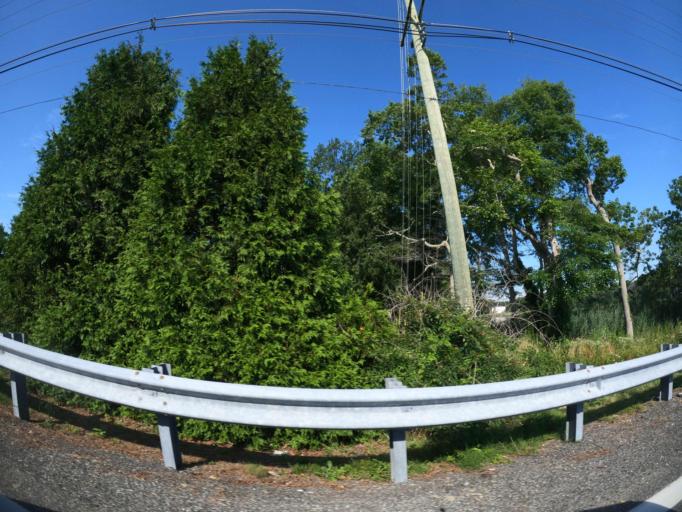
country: US
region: Delaware
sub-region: Sussex County
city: Ocean View
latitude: 38.4826
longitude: -75.1190
